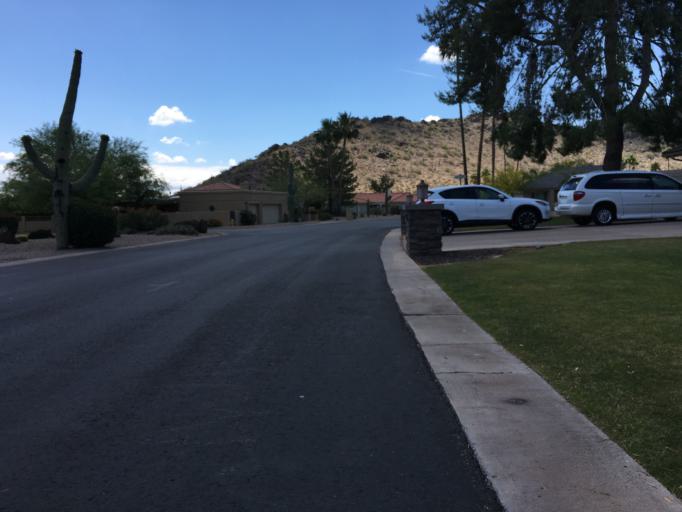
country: US
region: Arizona
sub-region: Maricopa County
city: Paradise Valley
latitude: 33.5763
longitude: -111.9886
